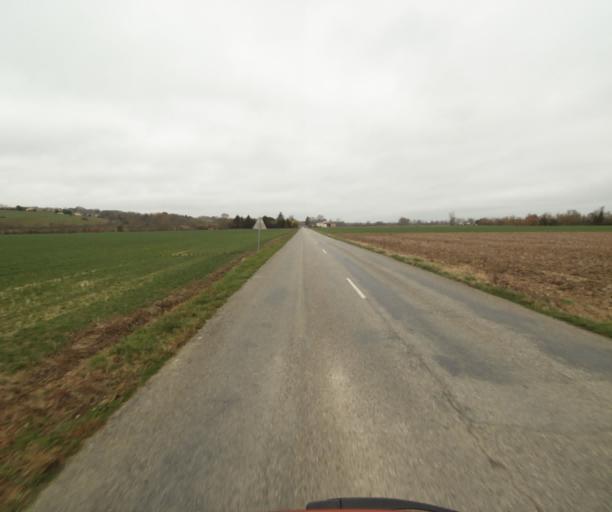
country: FR
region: Midi-Pyrenees
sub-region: Departement de la Haute-Garonne
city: Cintegabelle
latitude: 43.2620
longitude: 1.5275
